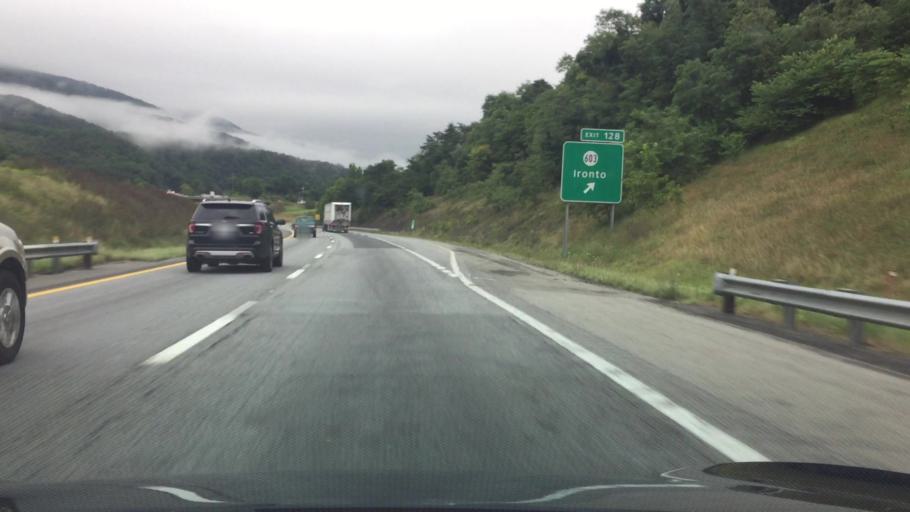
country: US
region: Virginia
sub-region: Montgomery County
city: Shawsville
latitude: 37.2293
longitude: -80.2407
